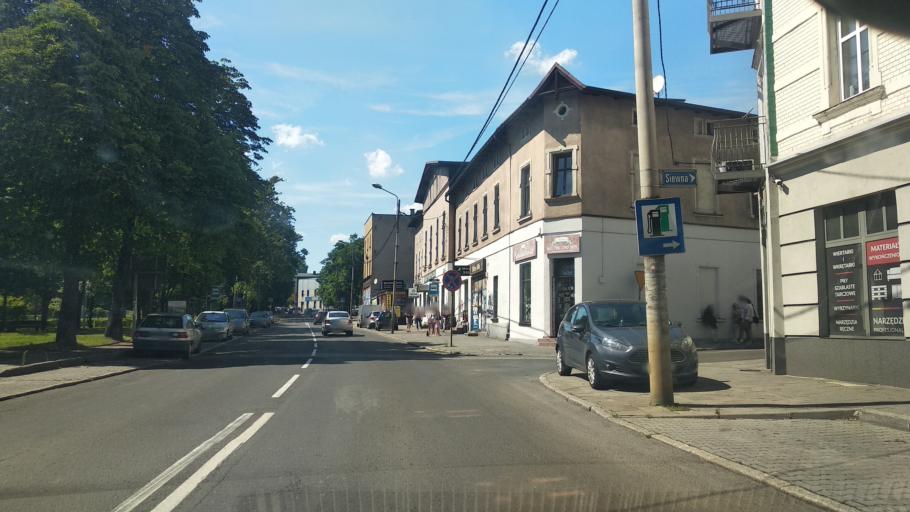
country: PL
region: Silesian Voivodeship
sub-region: Sosnowiec
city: Sosnowiec
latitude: 50.2686
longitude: 19.0813
